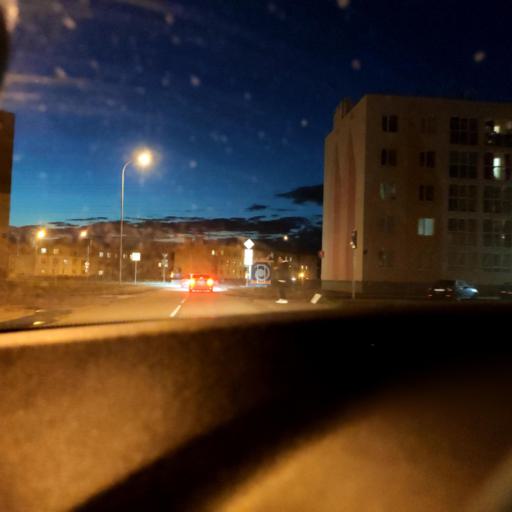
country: RU
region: Samara
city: Petra-Dubrava
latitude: 53.2960
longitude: 50.3187
